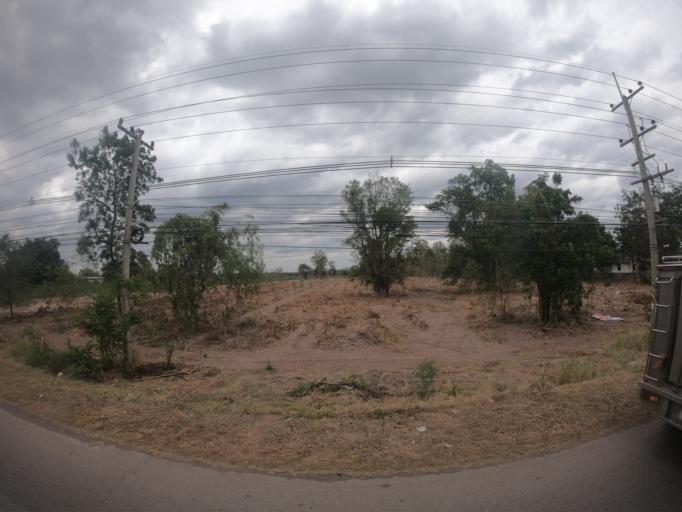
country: TH
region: Nakhon Ratchasima
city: Nakhon Ratchasima
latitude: 14.8772
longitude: 102.1762
